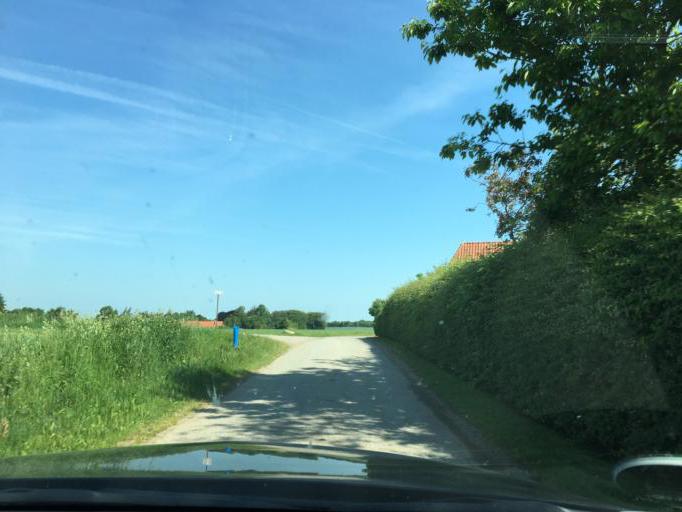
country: DK
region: South Denmark
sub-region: Kolding Kommune
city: Kolding
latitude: 55.5554
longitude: 9.4695
